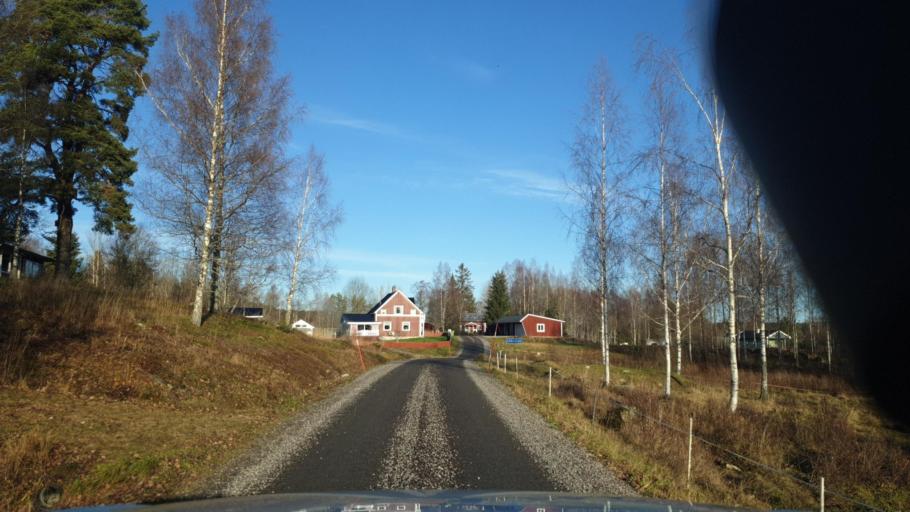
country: NO
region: Ostfold
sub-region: Romskog
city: Romskog
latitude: 59.8601
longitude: 11.9684
